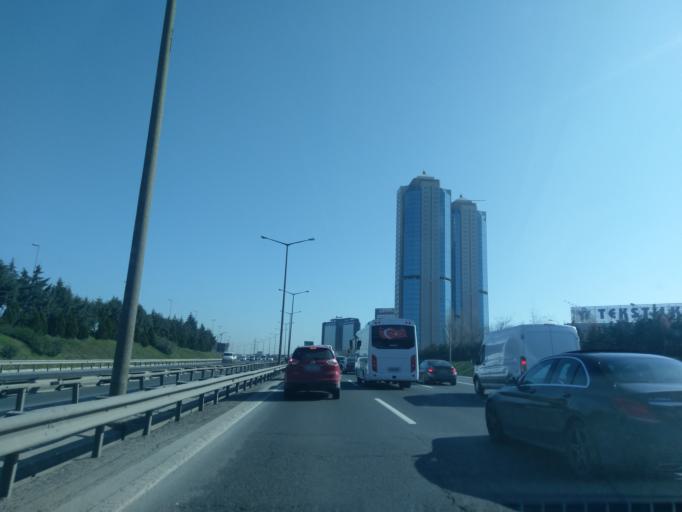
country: TR
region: Istanbul
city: Bagcilar
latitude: 41.0676
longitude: 28.8598
